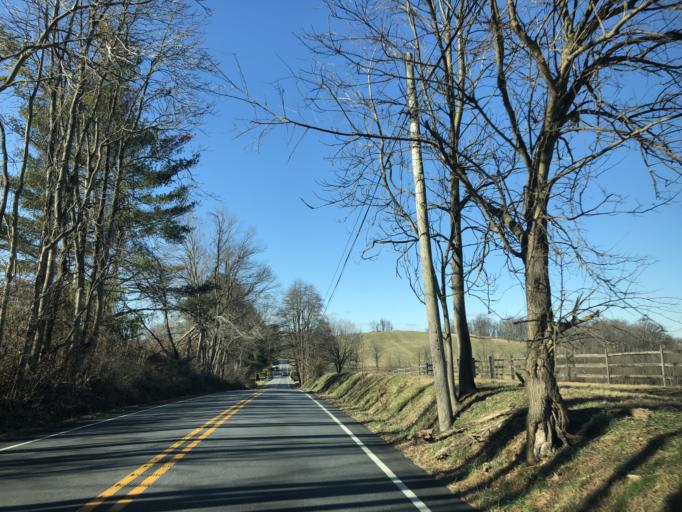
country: US
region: Pennsylvania
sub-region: Chester County
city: Upland
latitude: 39.9012
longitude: -75.7749
